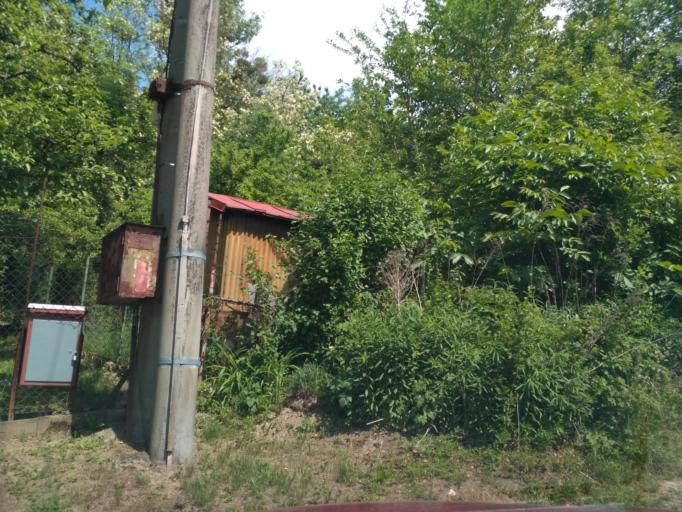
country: SK
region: Kosicky
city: Kosice
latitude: 48.7316
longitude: 21.2221
